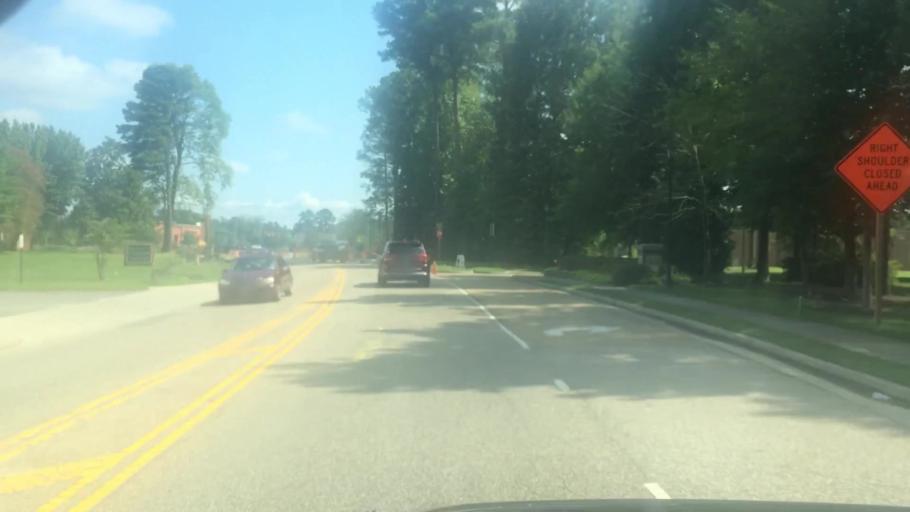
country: US
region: Virginia
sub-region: James City County
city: Williamsburg
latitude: 37.2892
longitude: -76.7292
